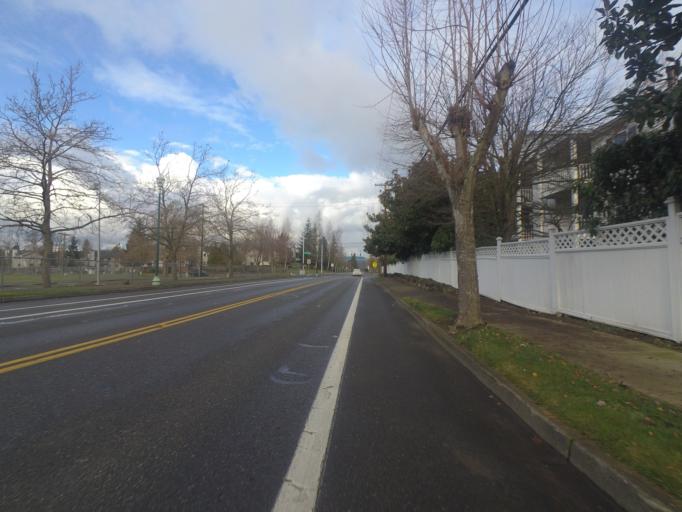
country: US
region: Washington
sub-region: Pierce County
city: University Place
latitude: 47.2346
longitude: -122.5504
